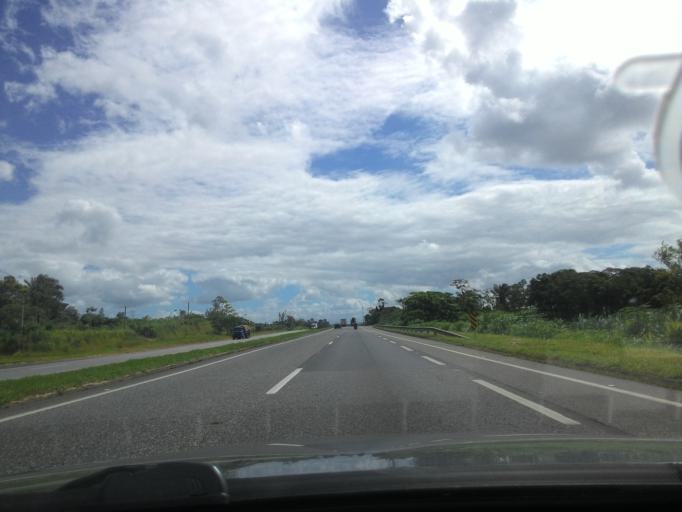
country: BR
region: Sao Paulo
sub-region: Pariquera-Acu
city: Pariquera Acu
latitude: -24.6322
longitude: -47.9059
